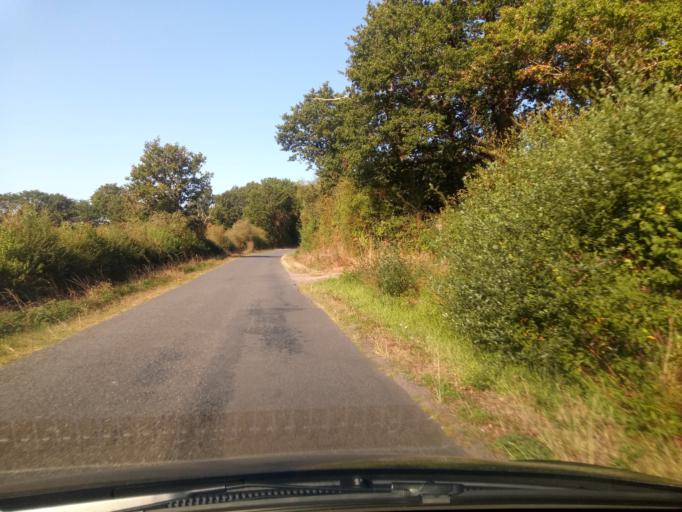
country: FR
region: Poitou-Charentes
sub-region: Departement de la Vienne
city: Saulge
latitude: 46.3313
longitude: 0.8214
